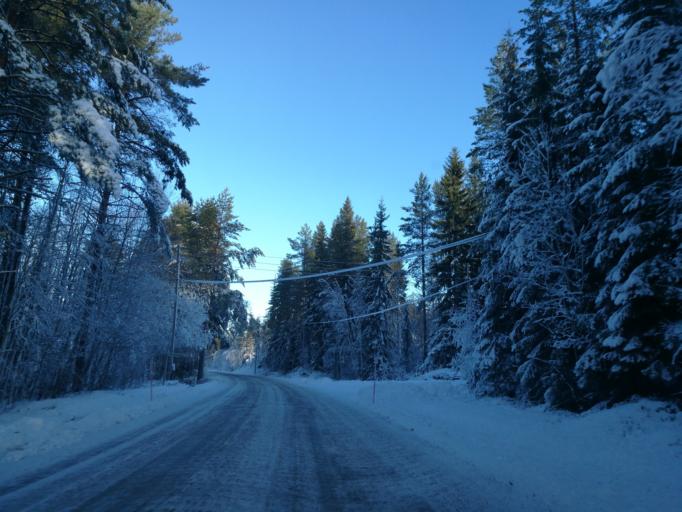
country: NO
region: Hedmark
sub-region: Grue
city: Kirkenaer
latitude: 60.4849
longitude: 12.5669
